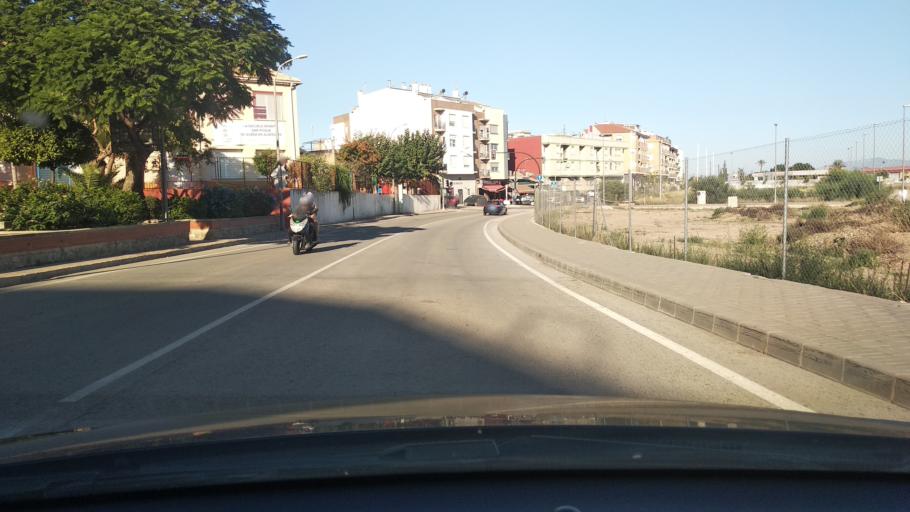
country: ES
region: Murcia
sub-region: Murcia
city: Murcia
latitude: 37.9420
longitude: -1.1159
